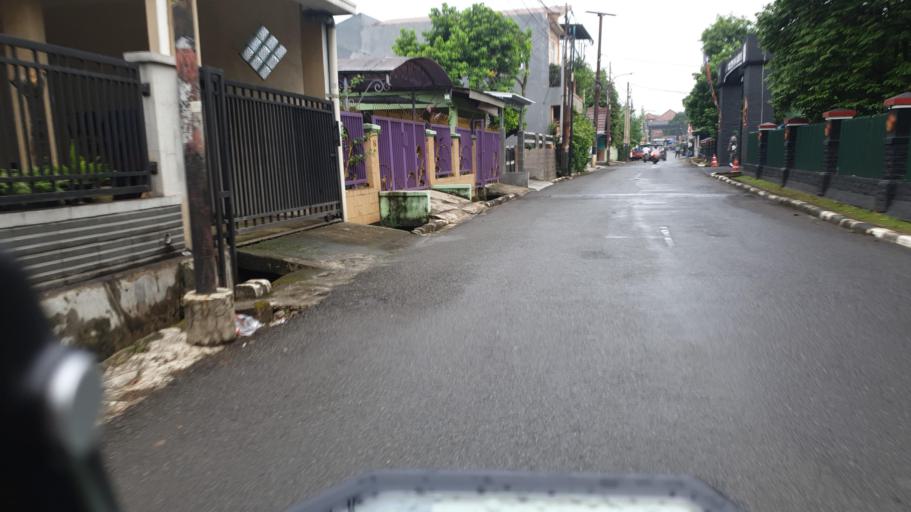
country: ID
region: West Java
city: Depok
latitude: -6.3435
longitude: 106.8300
